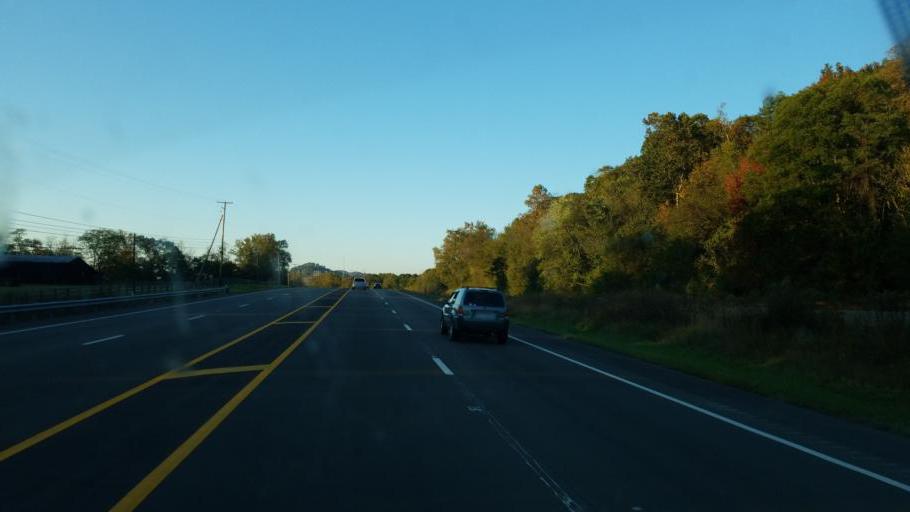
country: US
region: Ohio
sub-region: Scioto County
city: Lucasville
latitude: 38.8490
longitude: -82.9865
